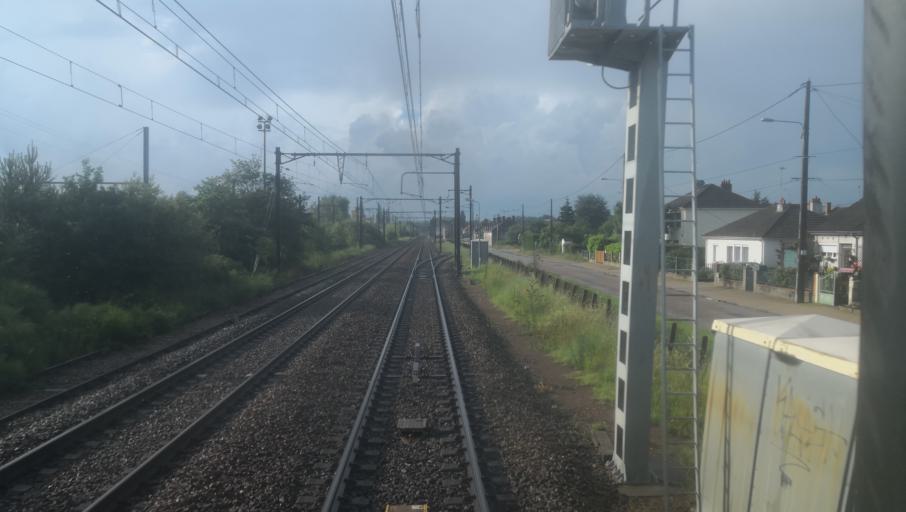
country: FR
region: Centre
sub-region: Departement du Loiret
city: La Ferte-Saint-Aubin
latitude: 47.7162
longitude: 1.9336
